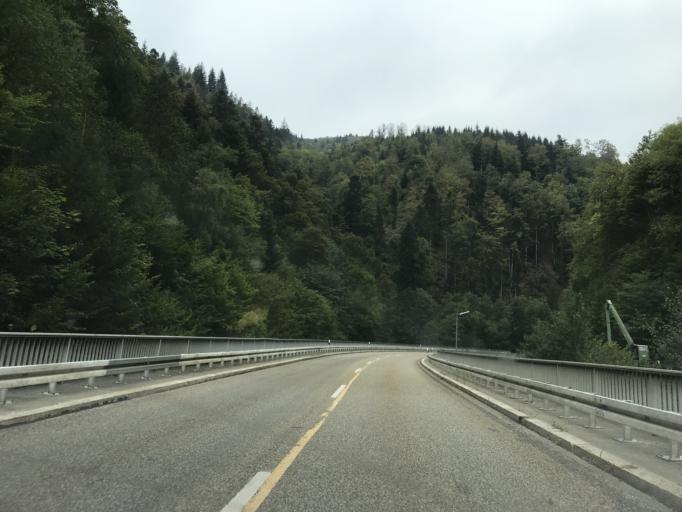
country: DE
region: Baden-Wuerttemberg
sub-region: Freiburg Region
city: Hasel
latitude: 47.6575
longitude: 7.9220
